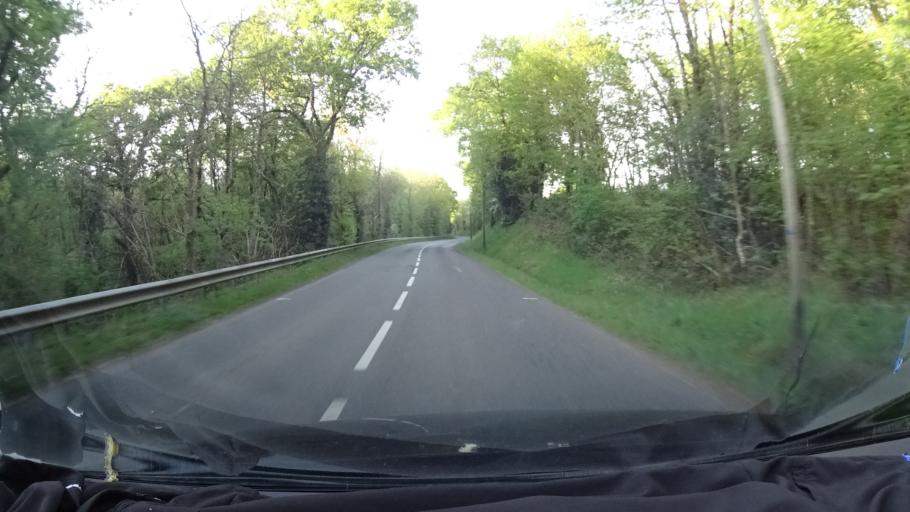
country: FR
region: Brittany
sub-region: Departement du Morbihan
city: Caden
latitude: 47.5957
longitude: -2.3089
